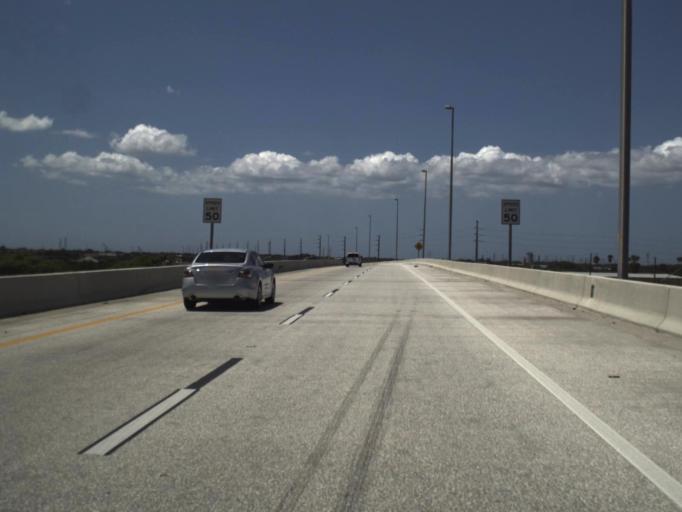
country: US
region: Florida
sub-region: Pinellas County
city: Feather Sound
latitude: 27.8784
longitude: -82.6764
